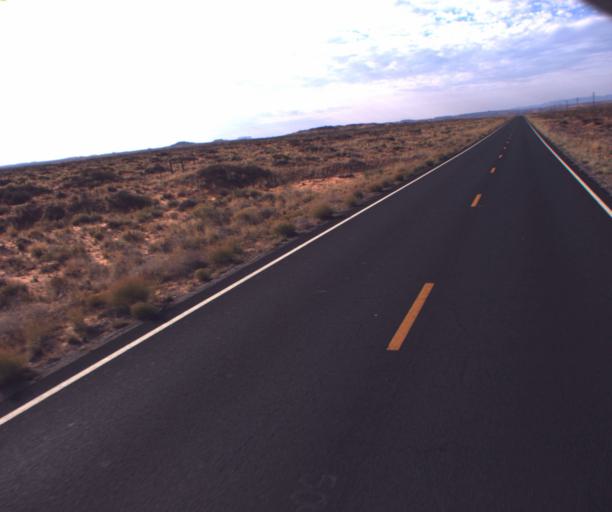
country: US
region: Arizona
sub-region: Apache County
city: Many Farms
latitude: 36.8493
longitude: -109.6389
